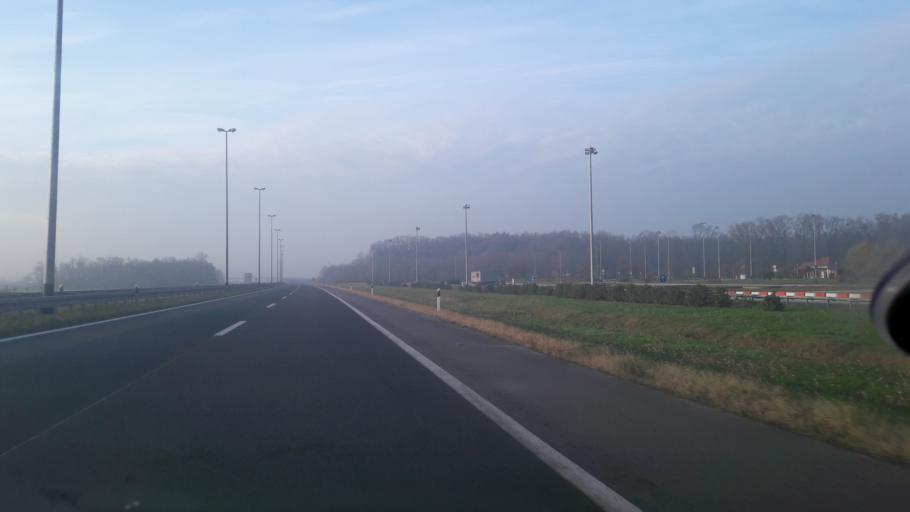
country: HR
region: Osjecko-Baranjska
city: Vuka
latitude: 45.4715
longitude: 18.4812
